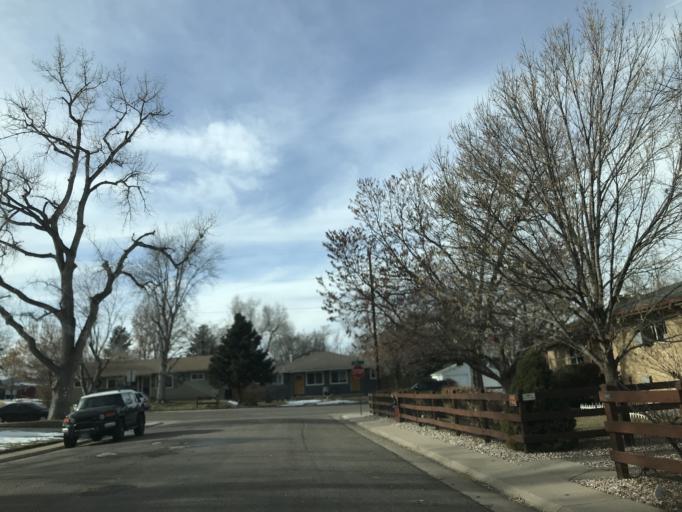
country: US
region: Colorado
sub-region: Arapahoe County
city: Littleton
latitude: 39.6019
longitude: -105.0131
